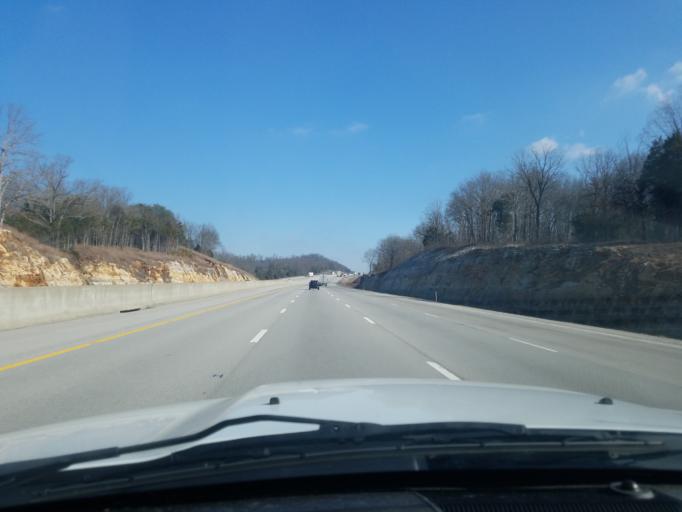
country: US
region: Kentucky
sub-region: Barren County
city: Cave City
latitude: 37.1004
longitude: -86.0512
